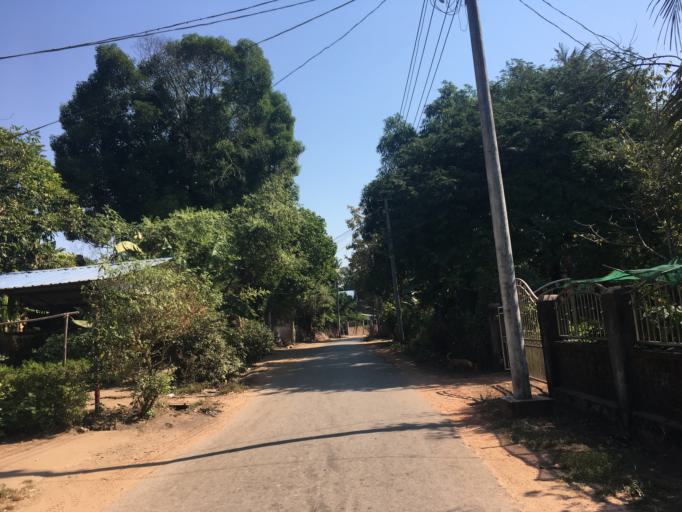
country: MM
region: Mon
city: Mawlamyine
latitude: 16.4322
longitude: 97.7011
